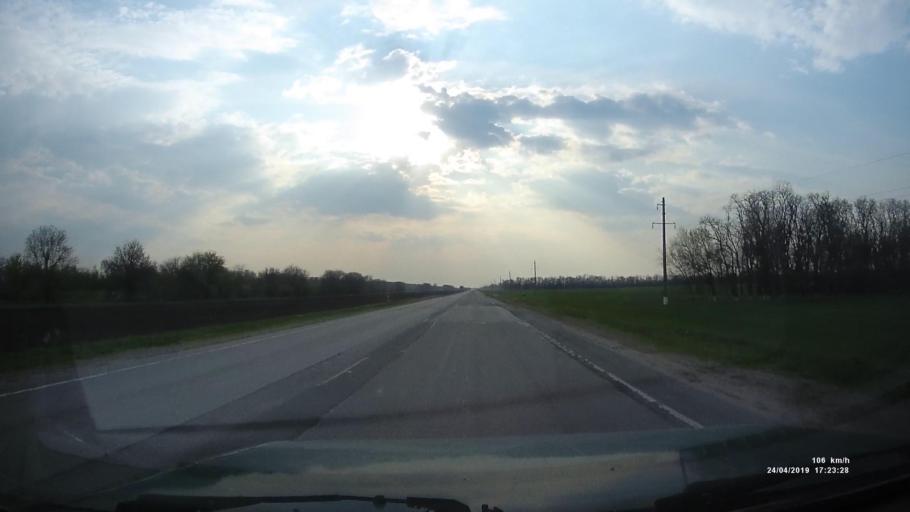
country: RU
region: Rostov
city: Gigant
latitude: 46.5219
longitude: 41.2852
